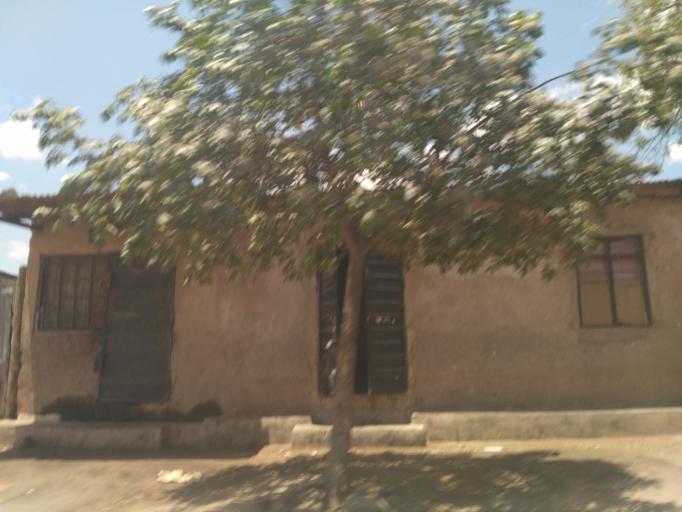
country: TZ
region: Dodoma
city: Dodoma
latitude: -6.1724
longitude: 35.7466
